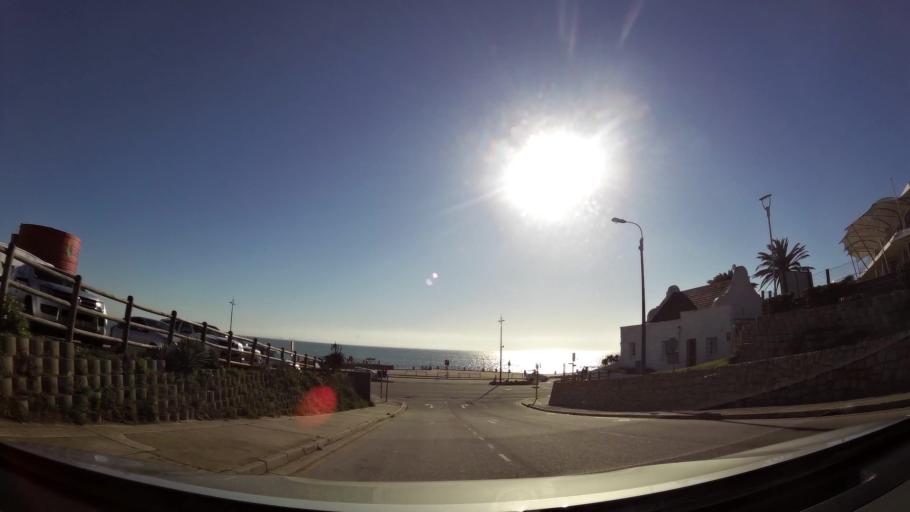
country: ZA
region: Eastern Cape
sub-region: Nelson Mandela Bay Metropolitan Municipality
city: Port Elizabeth
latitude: -33.9775
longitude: 25.6497
